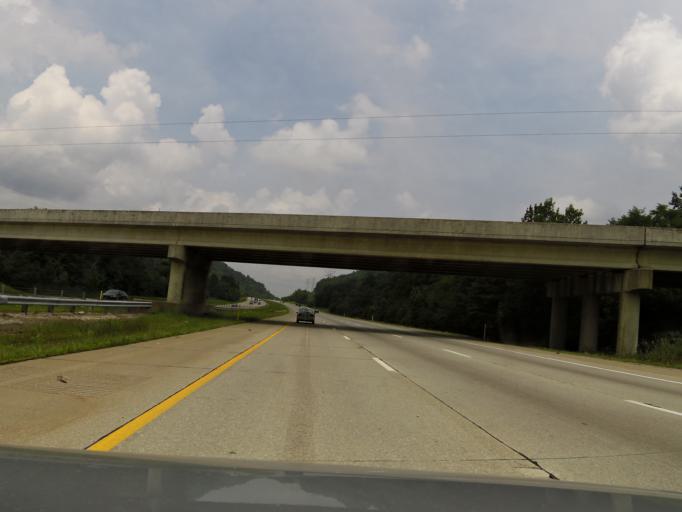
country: US
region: Kentucky
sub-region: Bullitt County
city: Lebanon Junction
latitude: 37.8714
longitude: -85.7037
